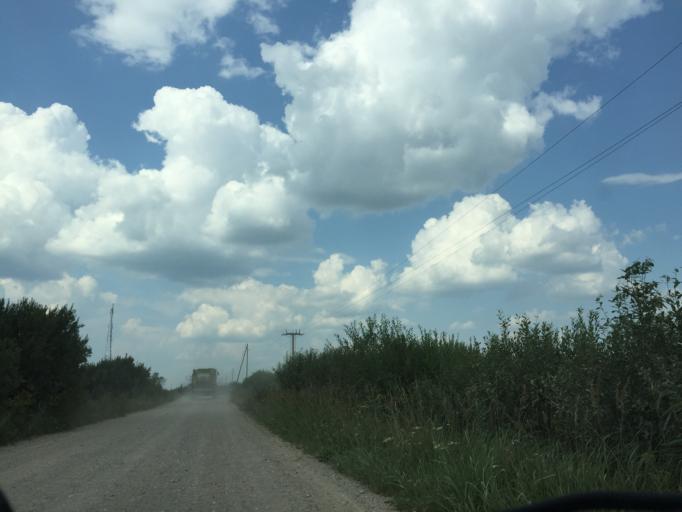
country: LT
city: Naujoji Akmene
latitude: 56.3492
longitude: 23.0596
